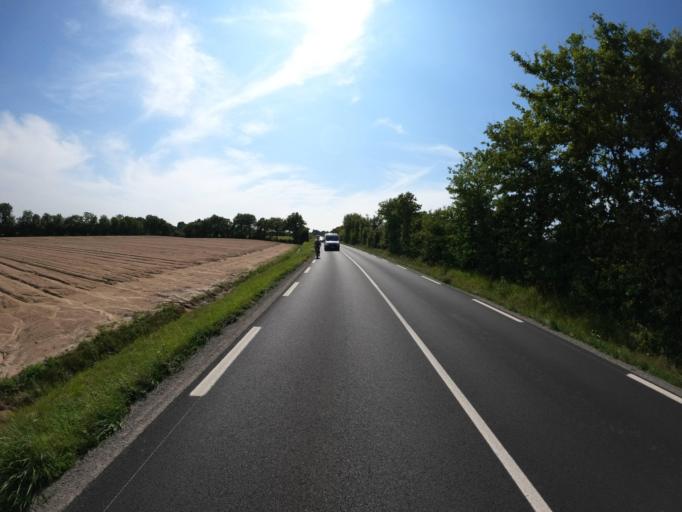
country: FR
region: Pays de la Loire
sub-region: Departement de la Loire-Atlantique
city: Saint-Meme-le-Tenu
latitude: 46.9927
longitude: -1.7752
